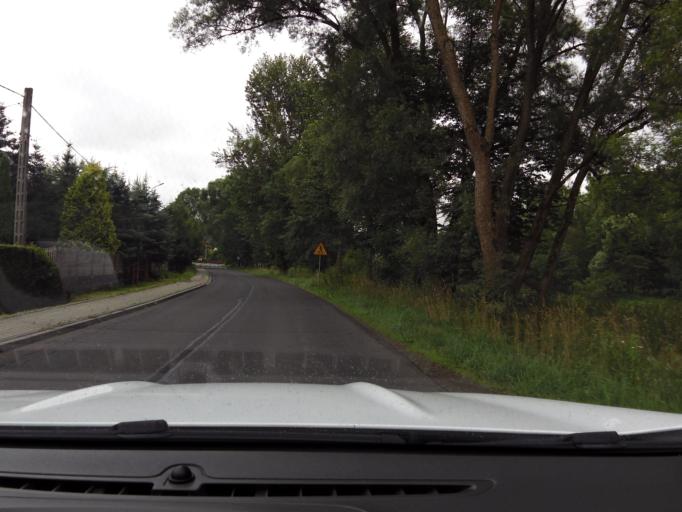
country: PL
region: Silesian Voivodeship
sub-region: Powiat zywiecki
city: Ujsoly
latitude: 49.4857
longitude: 19.1276
